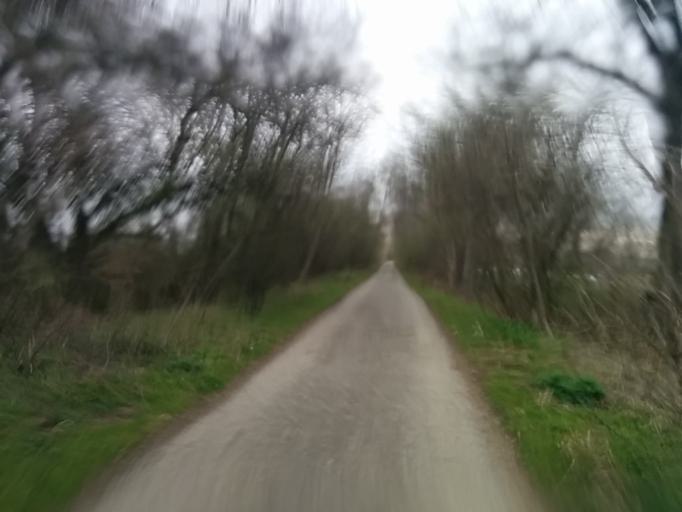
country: SK
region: Nitriansky
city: Sellye
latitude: 48.2394
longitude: 17.8236
